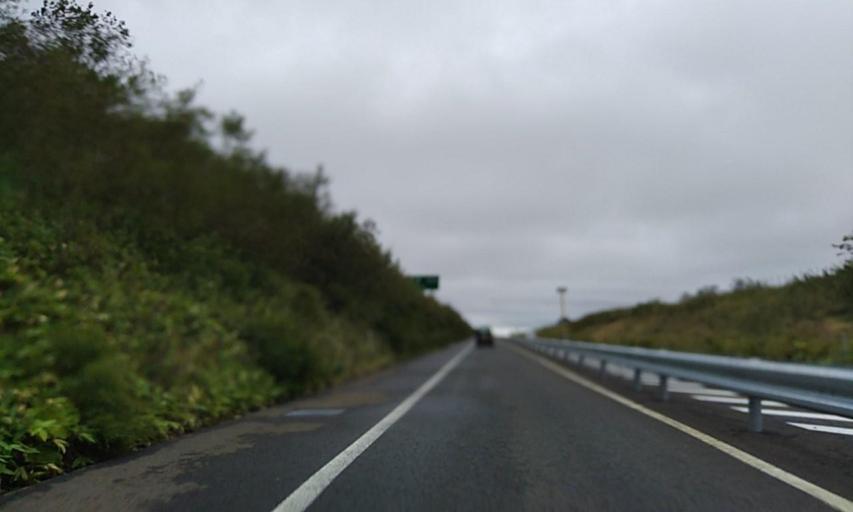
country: JP
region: Hokkaido
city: Nemuro
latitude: 43.3033
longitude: 145.5312
